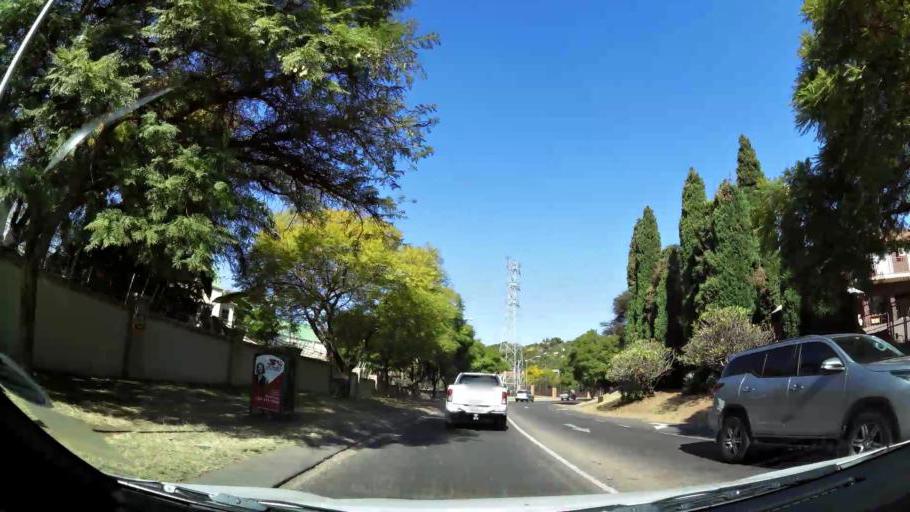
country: ZA
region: Gauteng
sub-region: City of Tshwane Metropolitan Municipality
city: Pretoria
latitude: -25.7985
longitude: 28.2715
